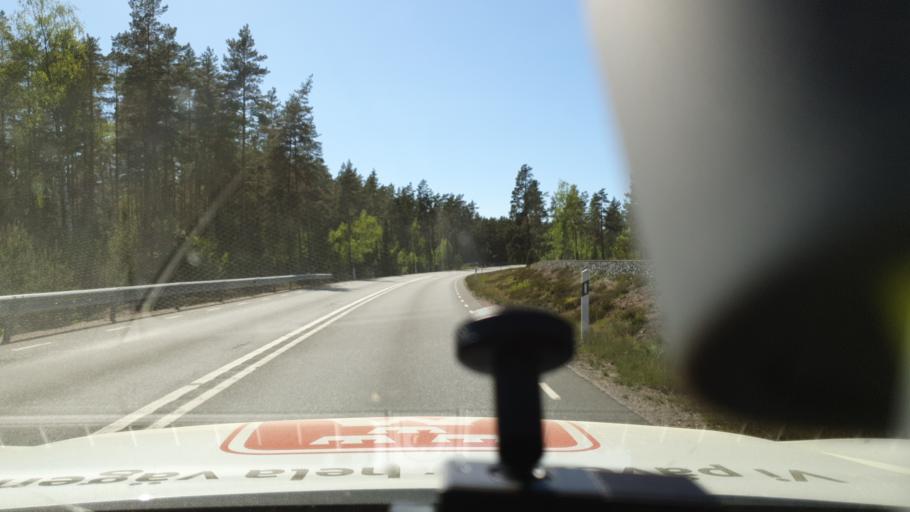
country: SE
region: Kronoberg
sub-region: Uppvidinge Kommun
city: Aseda
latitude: 57.3981
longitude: 15.3478
